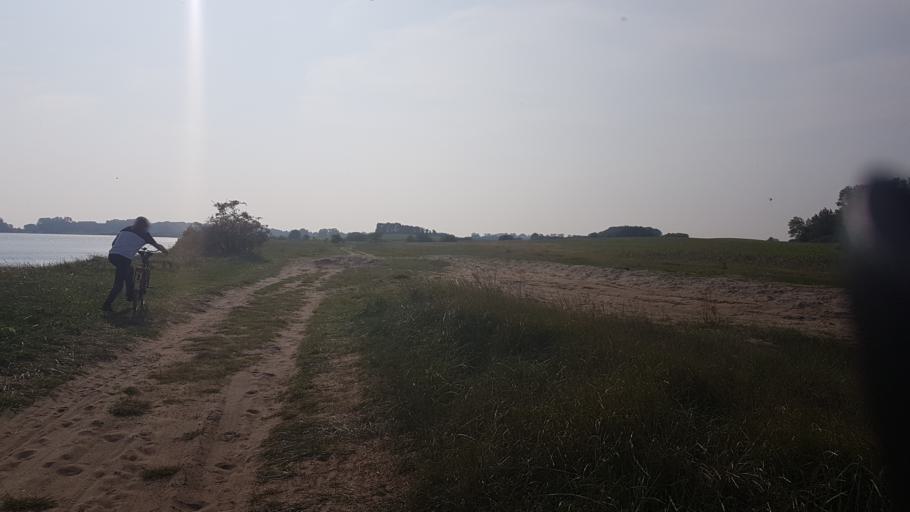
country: DE
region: Mecklenburg-Vorpommern
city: Garz
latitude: 54.3049
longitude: 13.4229
